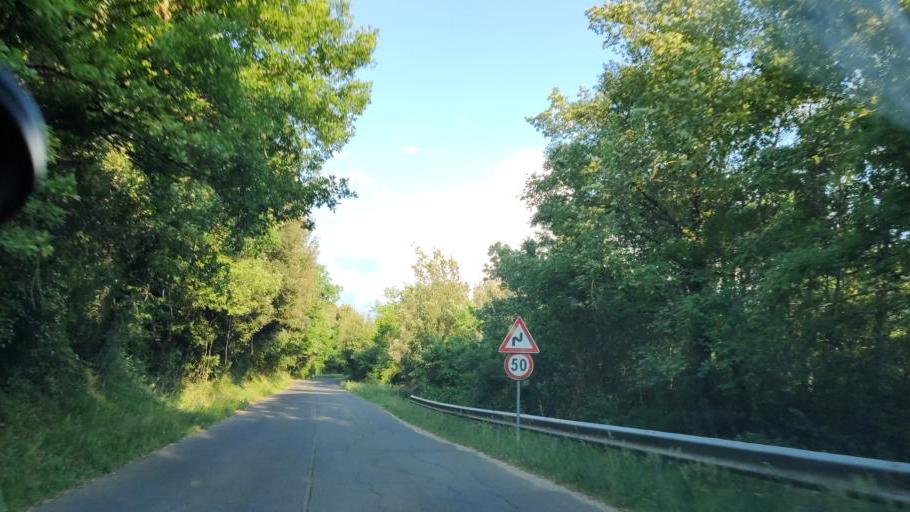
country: IT
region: Umbria
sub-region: Provincia di Terni
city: Lugnano in Teverina
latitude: 42.5871
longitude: 12.3780
